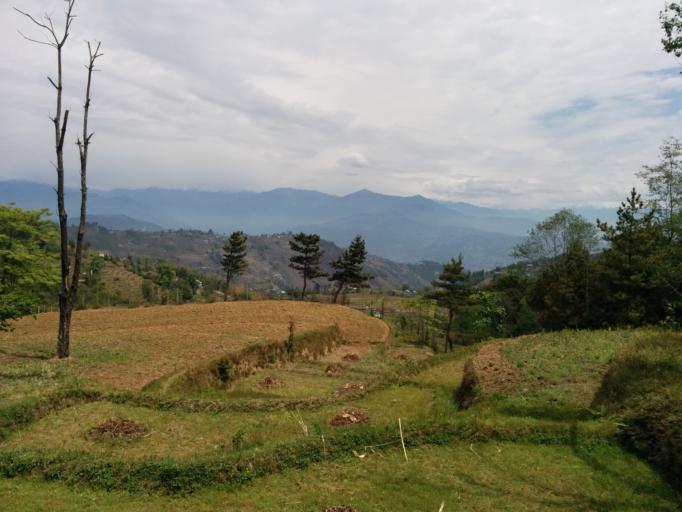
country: NP
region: Central Region
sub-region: Bagmati Zone
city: Nagarkot
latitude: 27.7398
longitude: 85.4982
